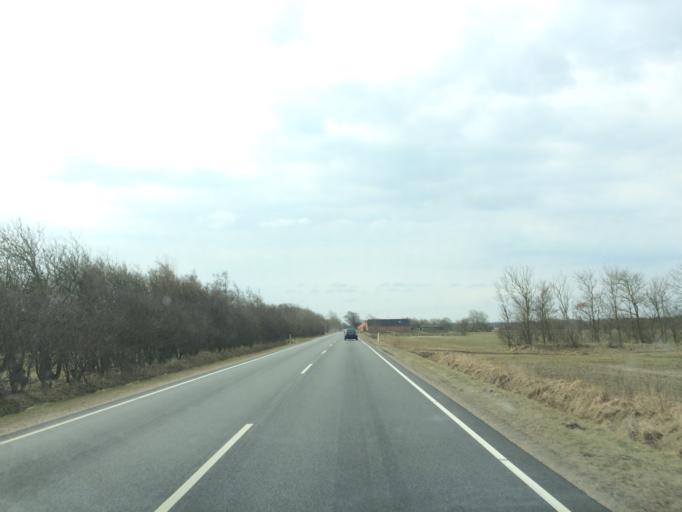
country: DK
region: Central Jutland
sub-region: Ringkobing-Skjern Kommune
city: Skjern
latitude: 55.9846
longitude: 8.5043
